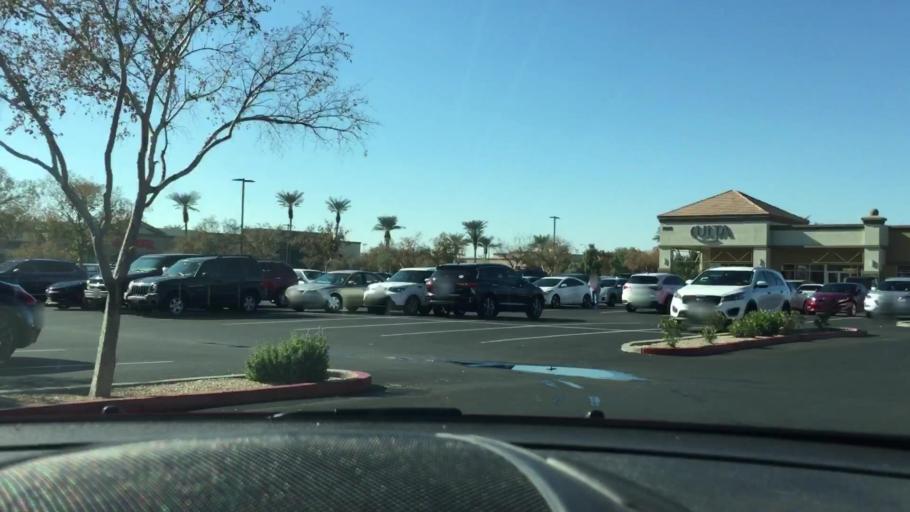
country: US
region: Arizona
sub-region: Maricopa County
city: Peoria
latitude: 33.6372
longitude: -112.2227
